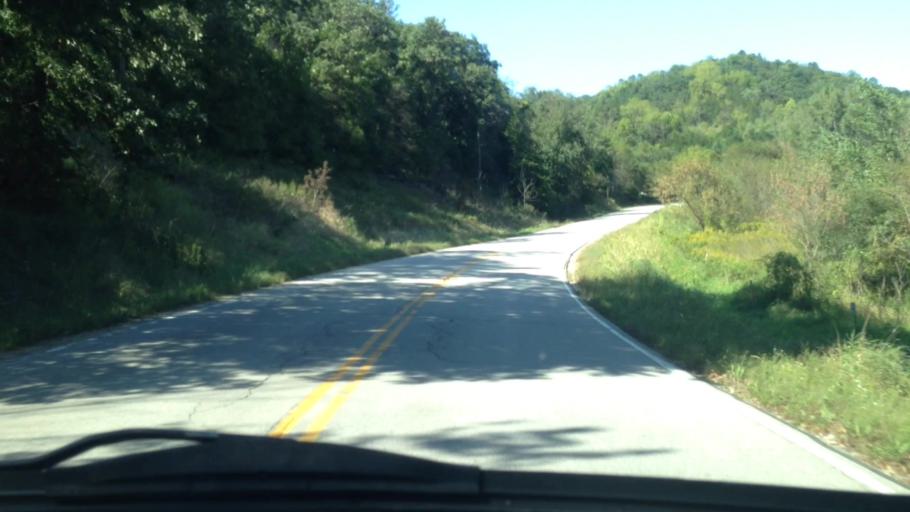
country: US
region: Minnesota
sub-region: Fillmore County
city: Rushford
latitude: 43.6713
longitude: -91.7928
